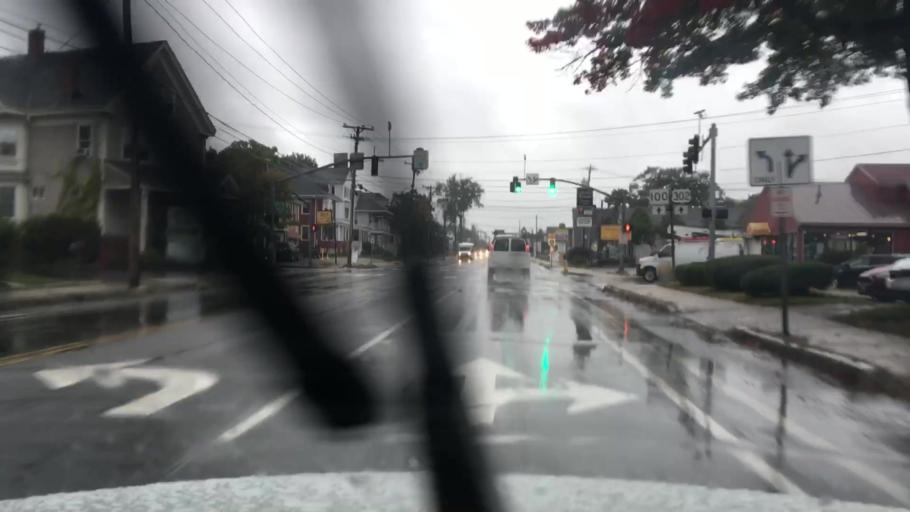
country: US
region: Maine
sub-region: Cumberland County
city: Portland
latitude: 43.6795
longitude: -70.2888
